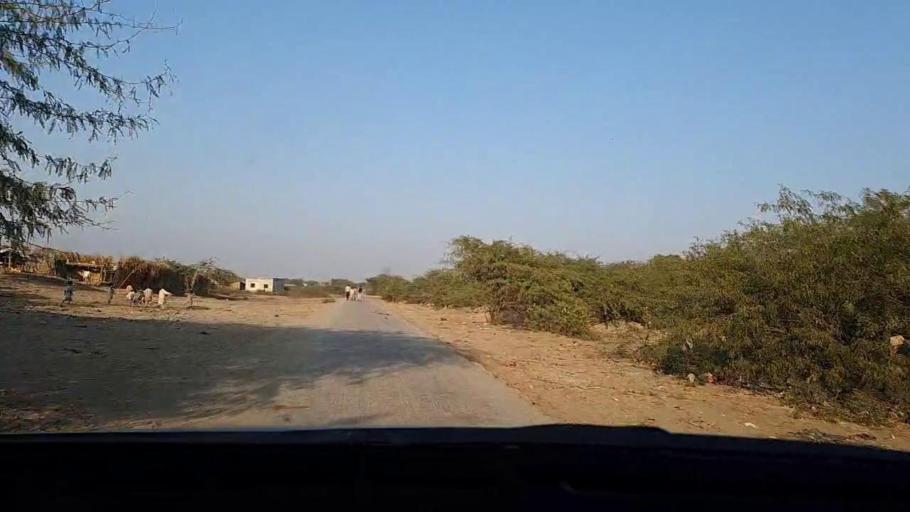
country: PK
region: Sindh
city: Tando Mittha Khan
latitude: 25.8667
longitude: 69.3077
